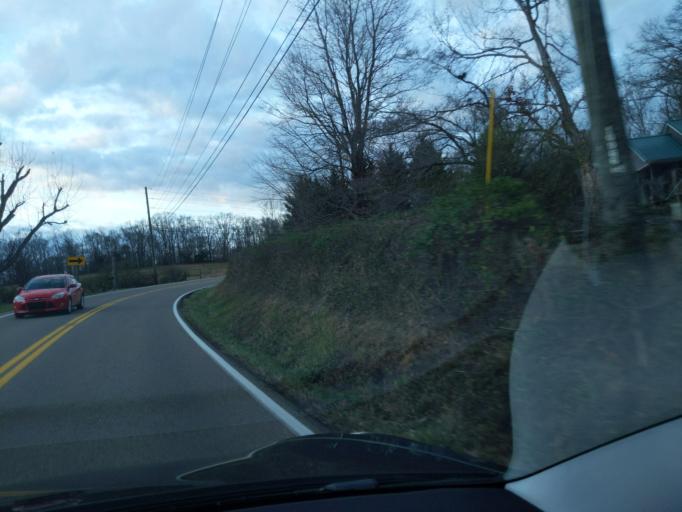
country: US
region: Tennessee
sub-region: Jefferson County
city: Dandridge
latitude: 36.0286
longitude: -83.4109
